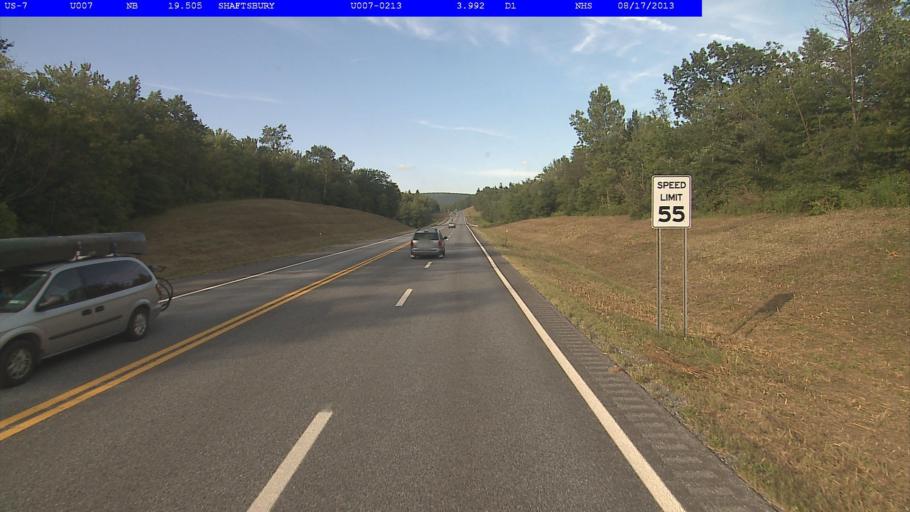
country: US
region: Vermont
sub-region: Bennington County
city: Arlington
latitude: 42.9831
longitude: -73.1518
